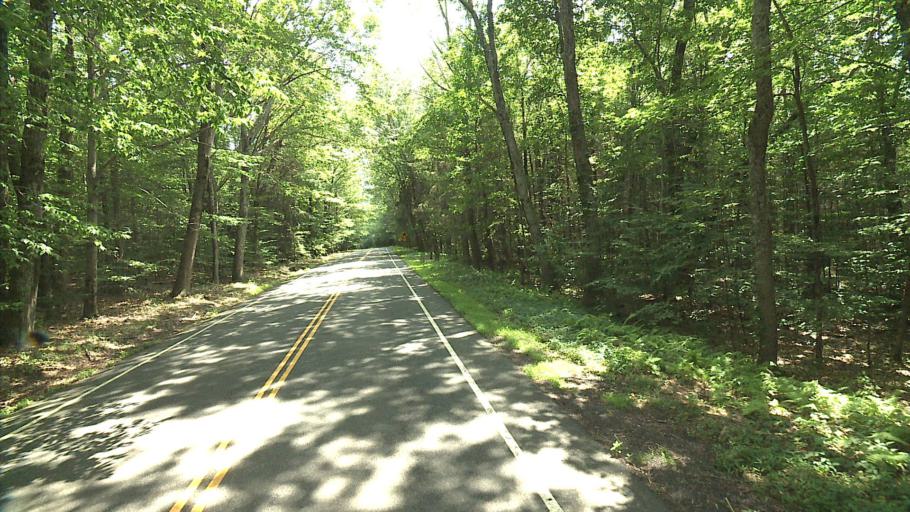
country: US
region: Massachusetts
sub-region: Hampden County
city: Granville
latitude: 42.0210
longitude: -72.9520
